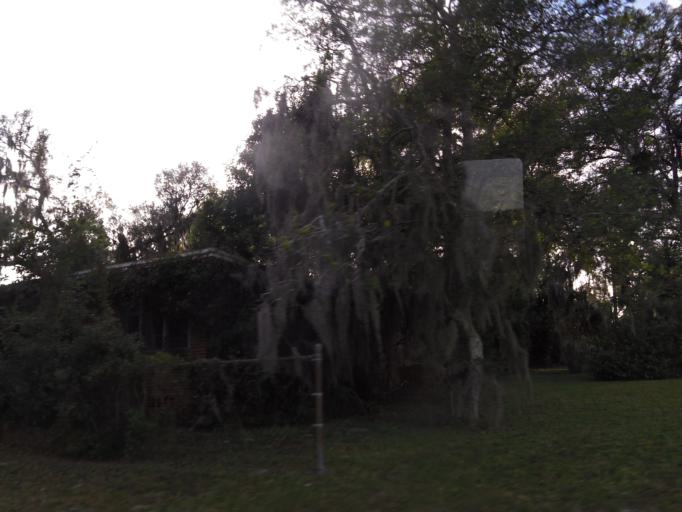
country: US
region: Florida
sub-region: Duval County
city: Jacksonville
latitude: 30.3914
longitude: -81.6590
